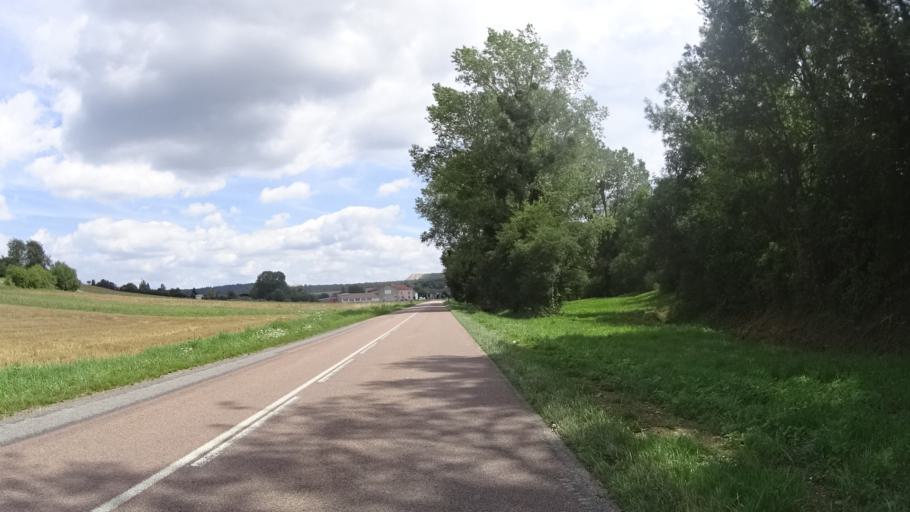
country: FR
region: Lorraine
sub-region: Departement de la Meuse
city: Euville
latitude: 48.7393
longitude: 5.6550
